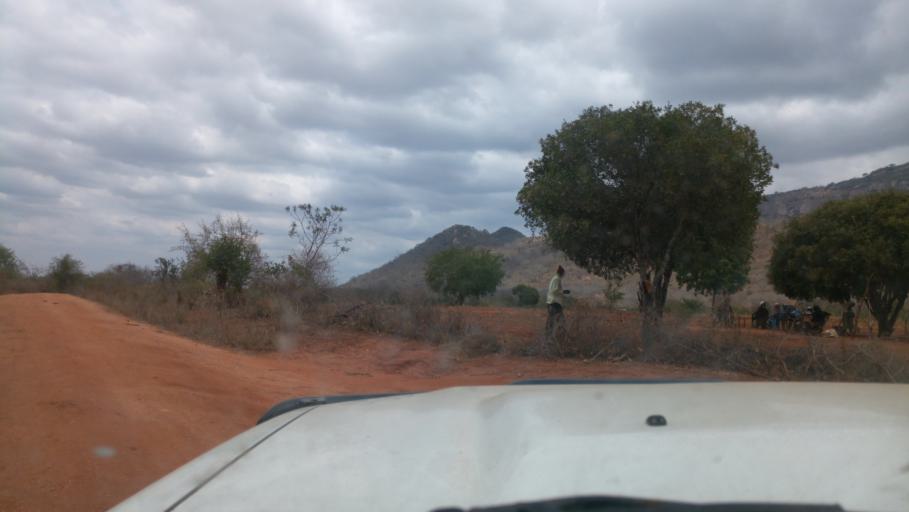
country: KE
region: Kitui
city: Kitui
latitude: -1.8810
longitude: 38.3750
